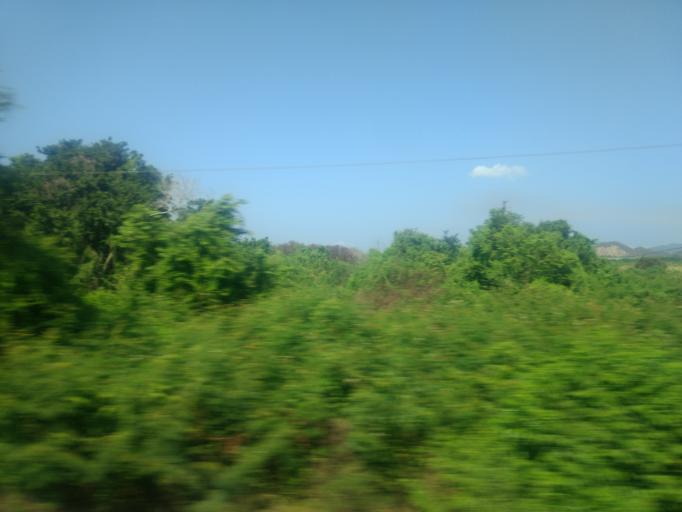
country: MX
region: Colima
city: El Colomo
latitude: 19.0454
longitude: -104.2614
